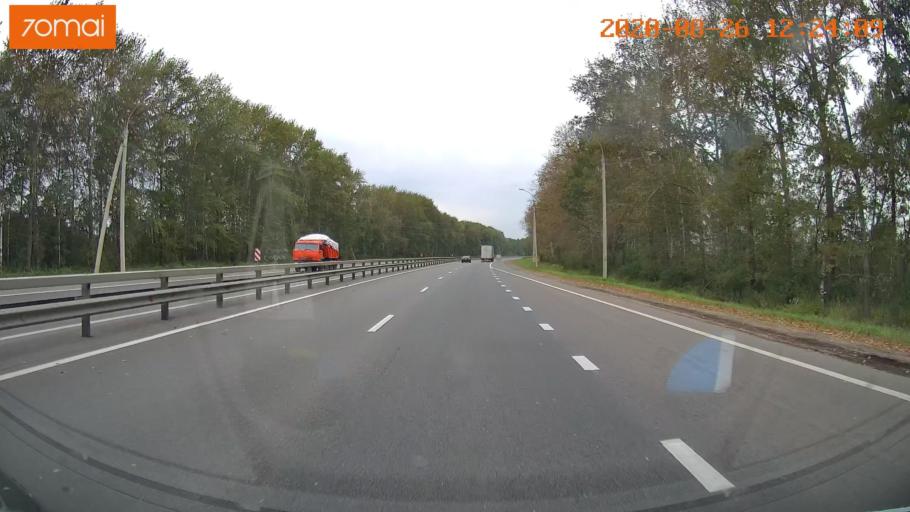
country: RU
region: Rjazan
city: Murmino
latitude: 54.5108
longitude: 39.8970
